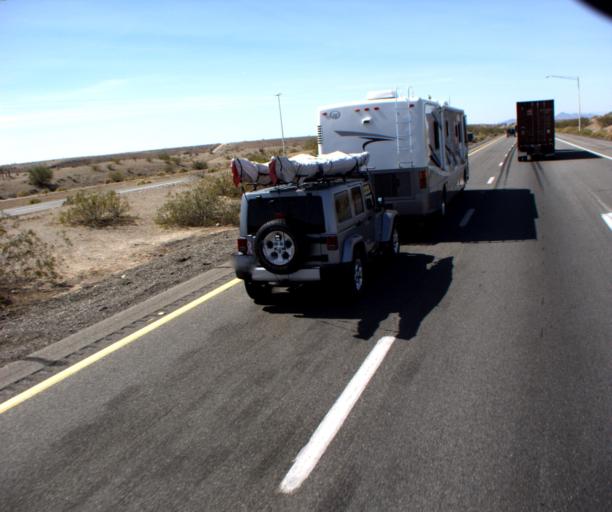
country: US
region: Arizona
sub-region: La Paz County
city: Ehrenberg
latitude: 33.6125
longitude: -114.4757
